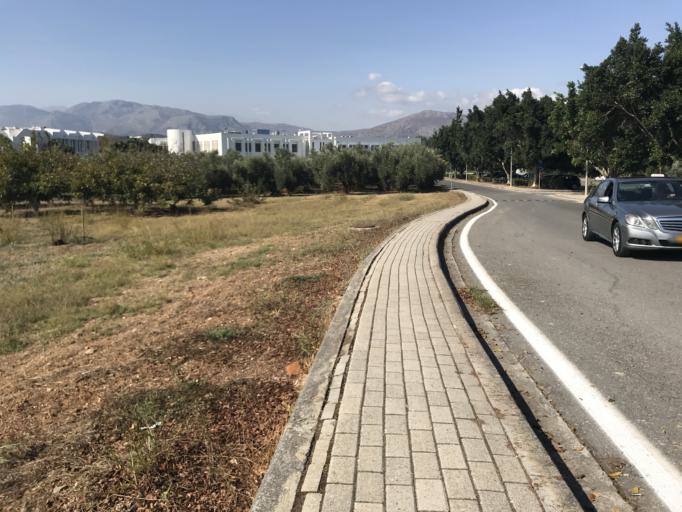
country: GR
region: Crete
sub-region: Nomos Irakleiou
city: Gazi
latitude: 35.3054
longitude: 25.0748
